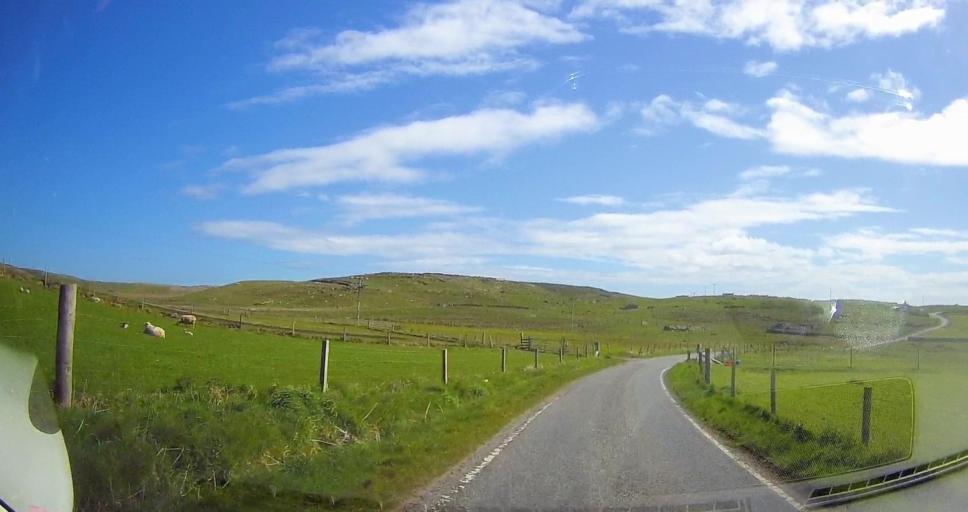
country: GB
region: Scotland
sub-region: Shetland Islands
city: Sandwick
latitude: 59.9427
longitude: -1.3224
